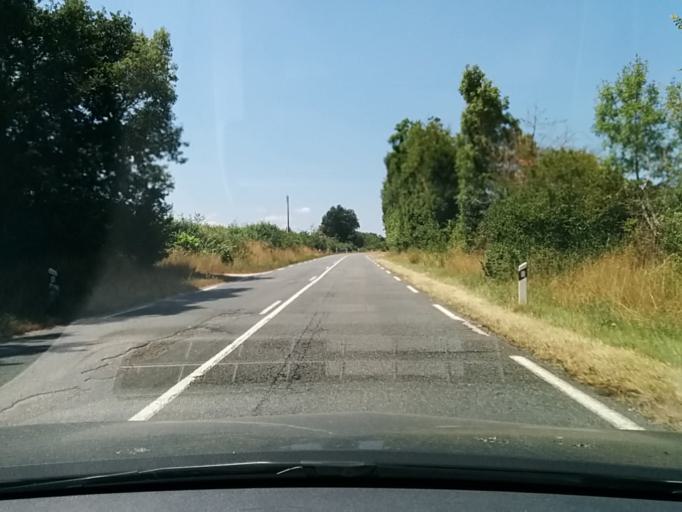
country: FR
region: Midi-Pyrenees
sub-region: Departement du Gers
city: Gimont
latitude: 43.6178
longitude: 0.9188
